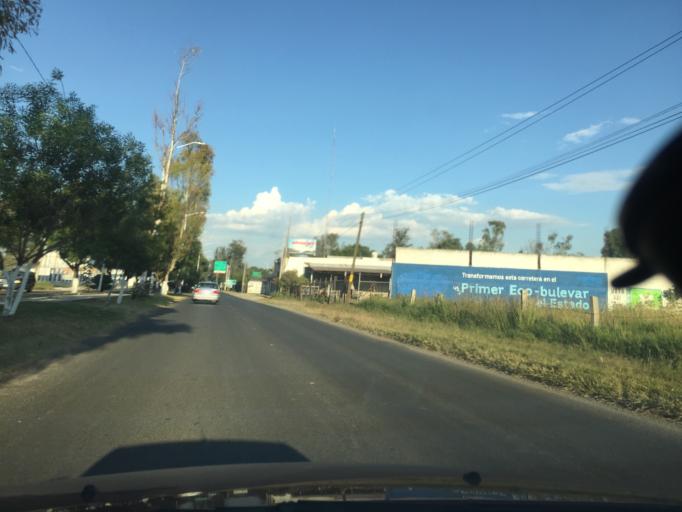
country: MX
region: Guanajuato
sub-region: San Francisco del Rincon
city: Estacion de San Francisco
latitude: 21.0315
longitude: -101.8314
